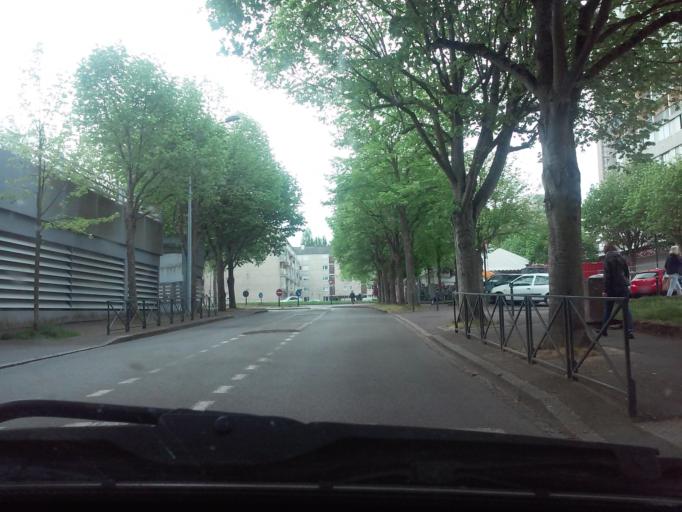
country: FR
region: Brittany
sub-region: Departement d'Ille-et-Vilaine
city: Rennes
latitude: 48.0916
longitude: -1.6804
